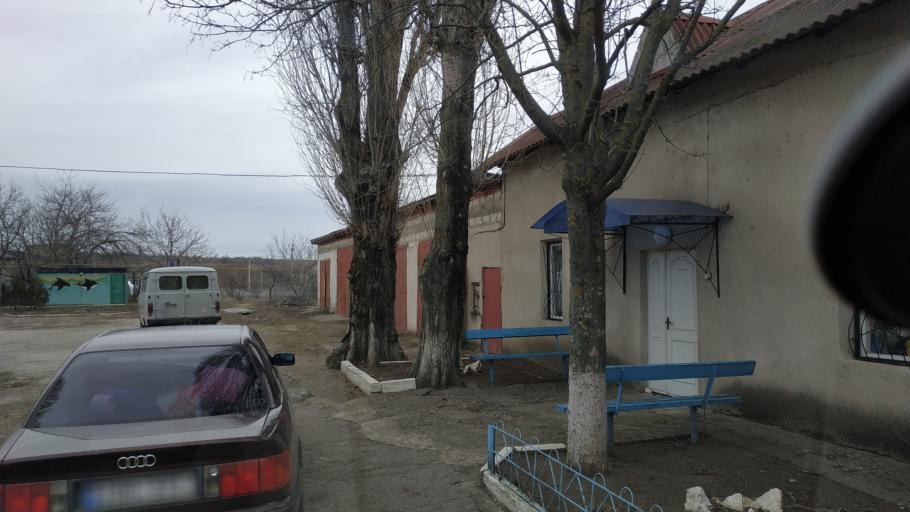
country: MD
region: Telenesti
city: Cocieri
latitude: 47.2932
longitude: 29.1216
